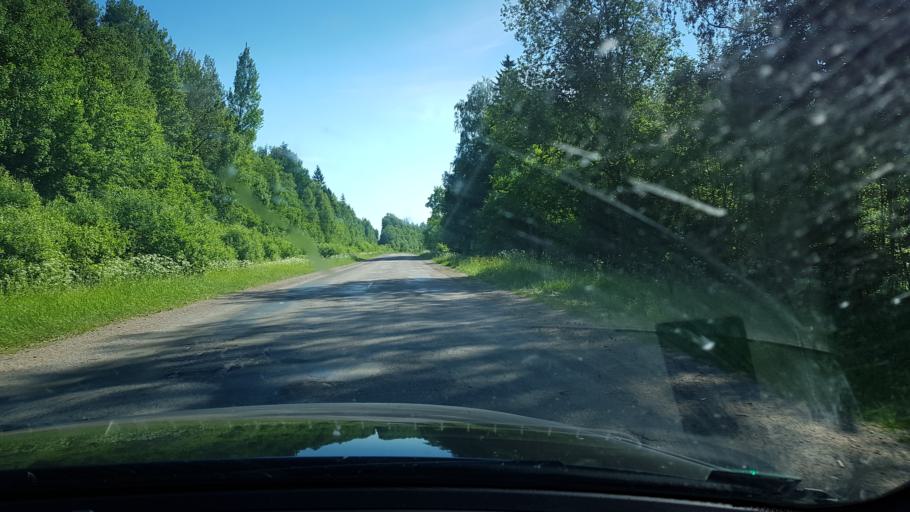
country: LV
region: Daugavpils
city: Daugavpils
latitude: 55.8192
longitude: 26.7476
